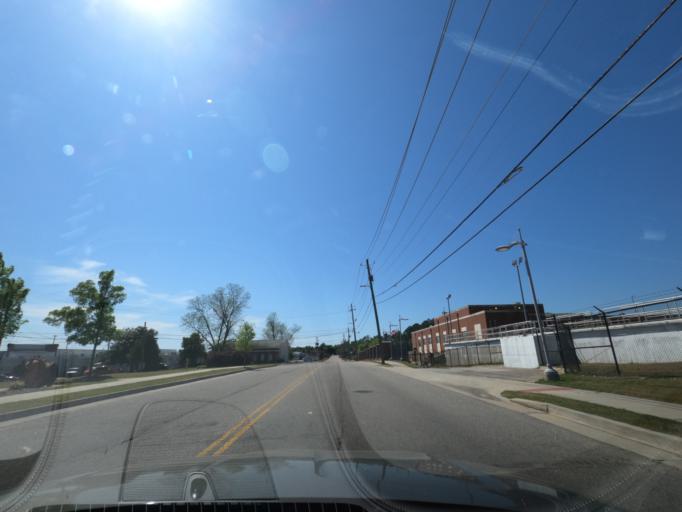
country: US
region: Georgia
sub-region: Richmond County
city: Augusta
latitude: 33.4711
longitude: -82.0334
